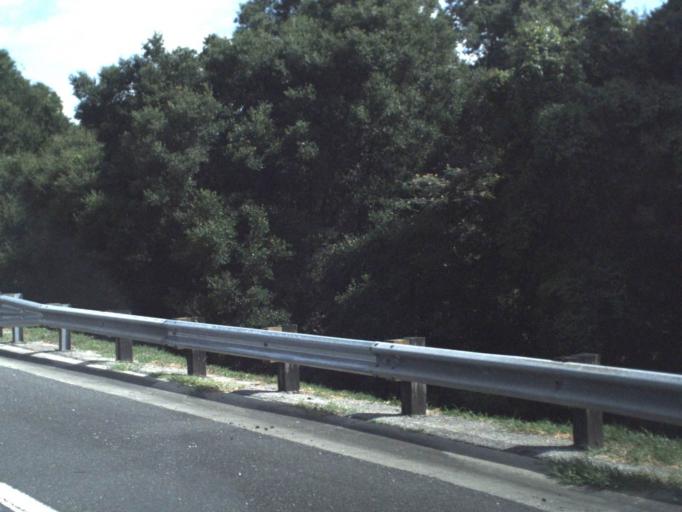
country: US
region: Florida
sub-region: Alachua County
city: Alachua
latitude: 29.7881
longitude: -82.4784
